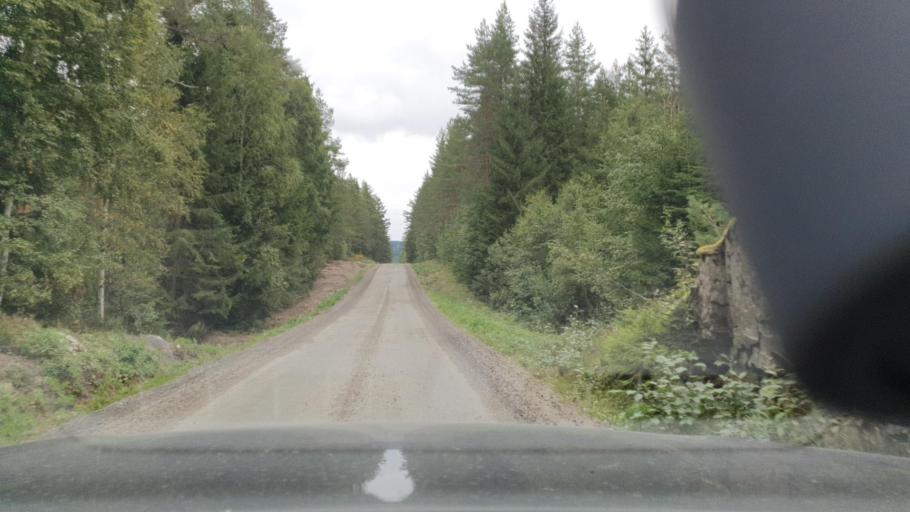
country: SE
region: Vaermland
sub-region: Torsby Kommun
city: Torsby
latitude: 60.3818
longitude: 12.8788
